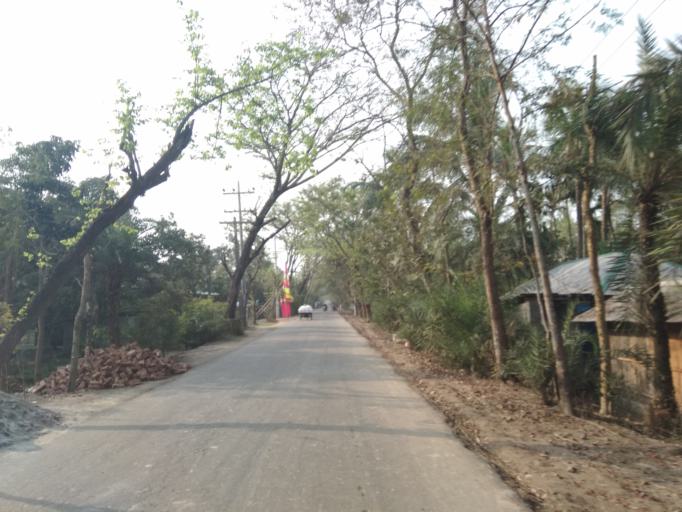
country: IN
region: West Bengal
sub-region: North 24 Parganas
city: Taki
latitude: 22.3255
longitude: 89.1055
